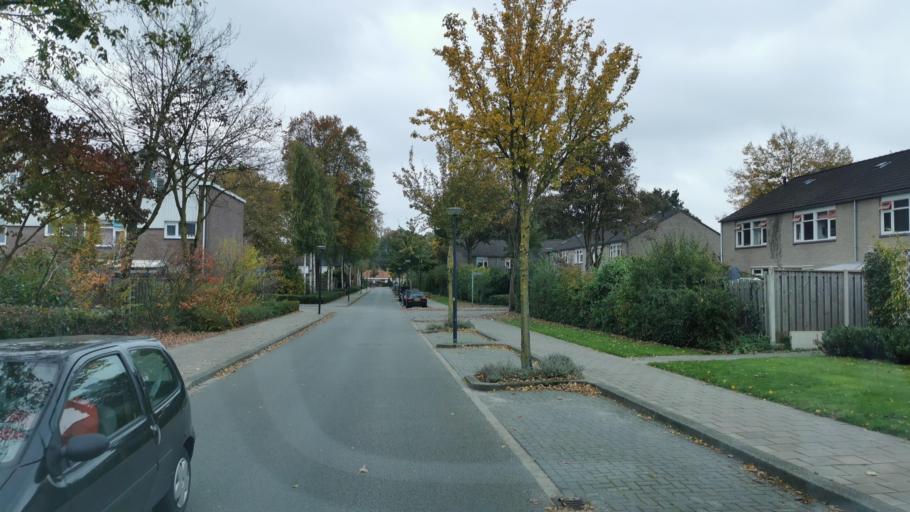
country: DE
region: North Rhine-Westphalia
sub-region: Regierungsbezirk Munster
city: Gronau
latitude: 52.2102
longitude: 6.9680
